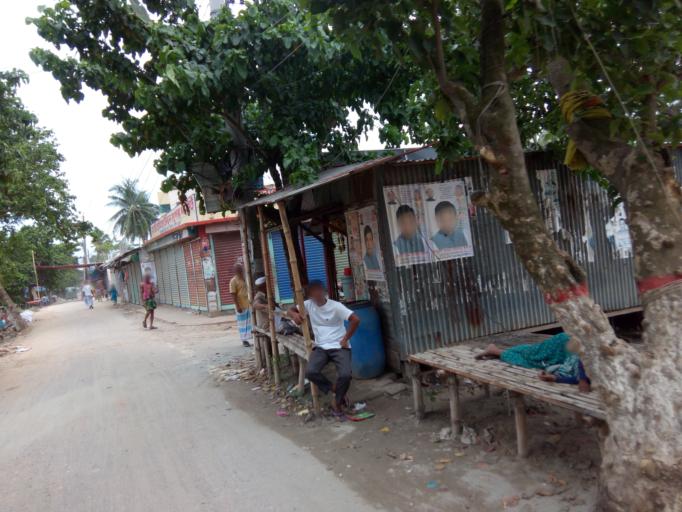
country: BD
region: Dhaka
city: Paltan
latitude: 23.7557
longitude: 90.4561
